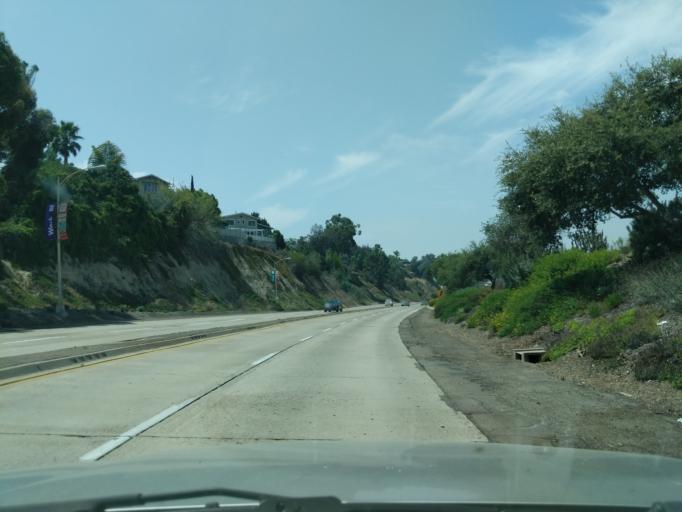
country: US
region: California
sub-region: San Diego County
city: San Diego
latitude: 32.7485
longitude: -117.1744
